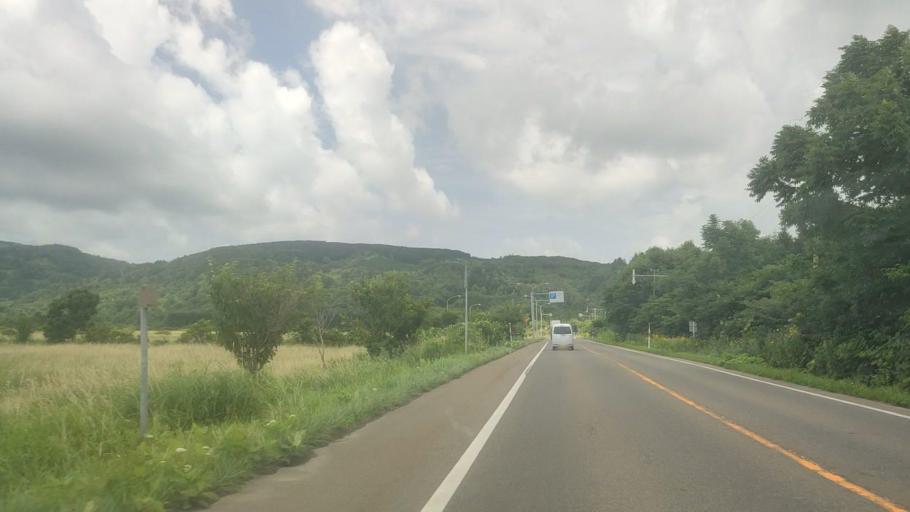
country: JP
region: Hokkaido
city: Niseko Town
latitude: 42.5846
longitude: 140.4512
